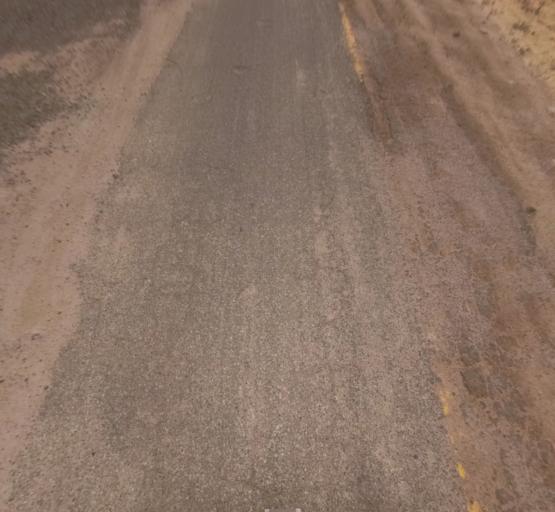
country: US
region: California
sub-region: Madera County
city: Madera Acres
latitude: 37.0026
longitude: -120.0660
